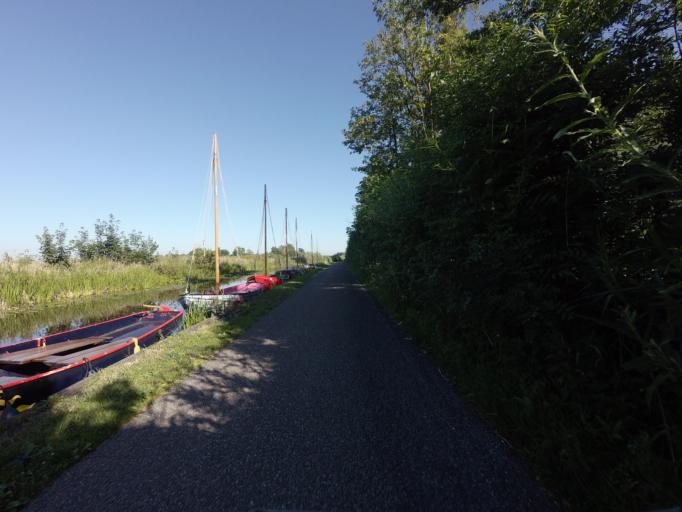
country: NL
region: South Holland
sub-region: Bodegraven-Reeuwijk
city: Reeuwijk
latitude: 52.0210
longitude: 4.7458
